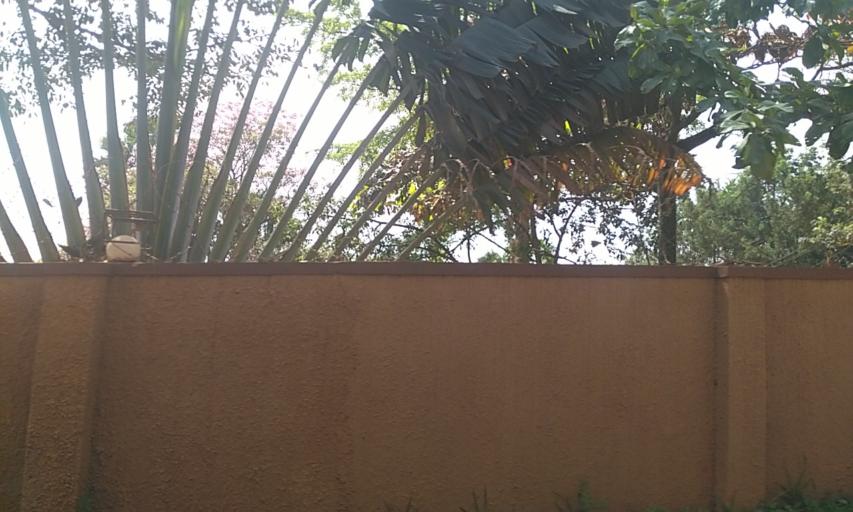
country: UG
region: Central Region
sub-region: Wakiso District
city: Kireka
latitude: 0.3513
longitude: 32.6117
